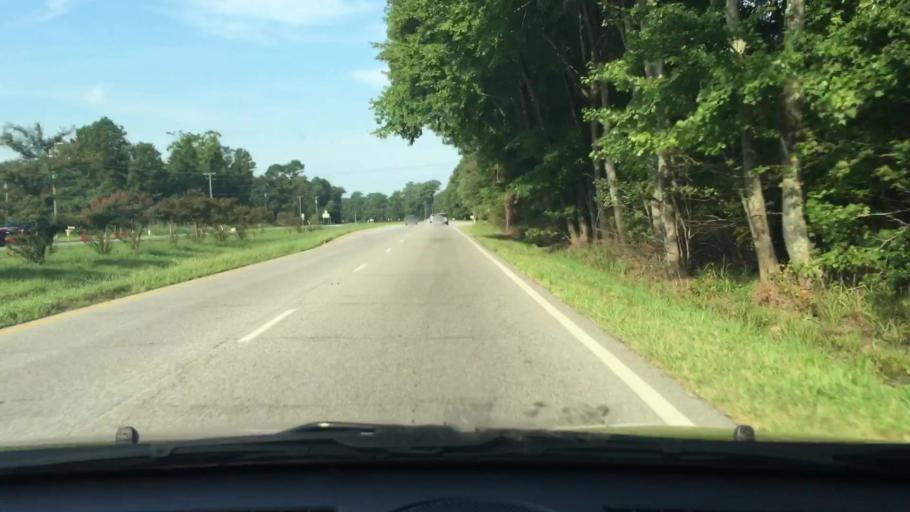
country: US
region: Virginia
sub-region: Isle of Wight County
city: Carrollton
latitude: 36.9409
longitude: -76.5686
